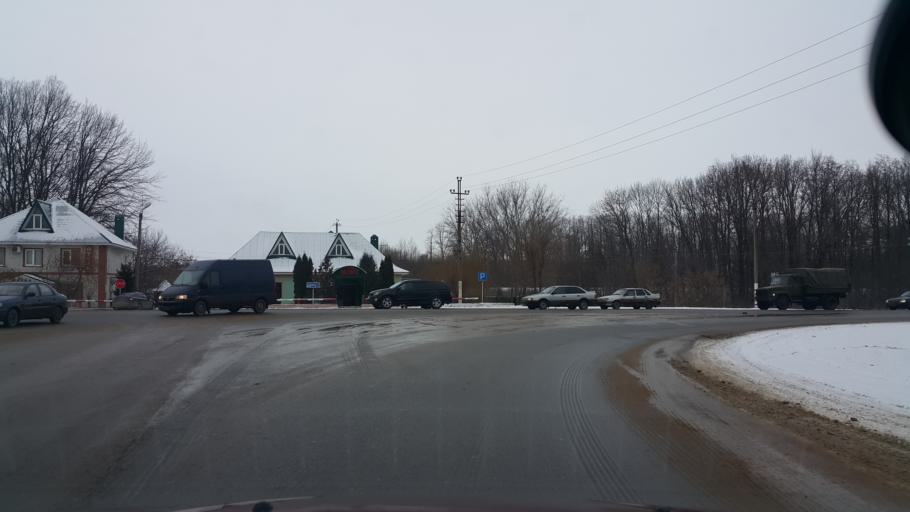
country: RU
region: Tambov
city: Bokino
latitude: 52.6168
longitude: 41.4444
